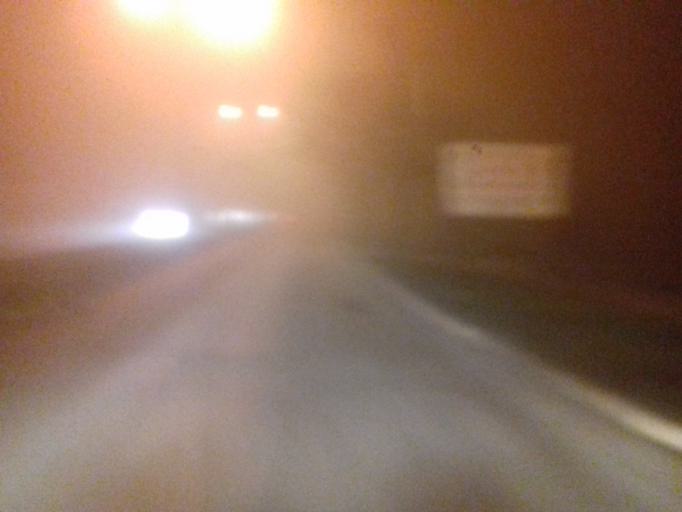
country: BA
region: Federation of Bosnia and Herzegovina
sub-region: Kanton Sarajevo
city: Sarajevo
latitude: 43.8303
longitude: 18.3560
